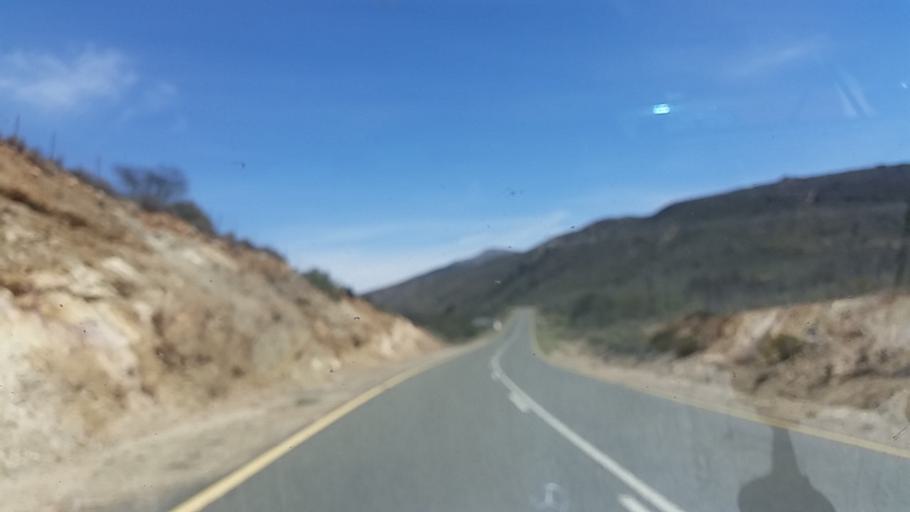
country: ZA
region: Eastern Cape
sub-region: Cacadu District Municipality
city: Willowmore
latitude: -33.3882
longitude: 23.3888
